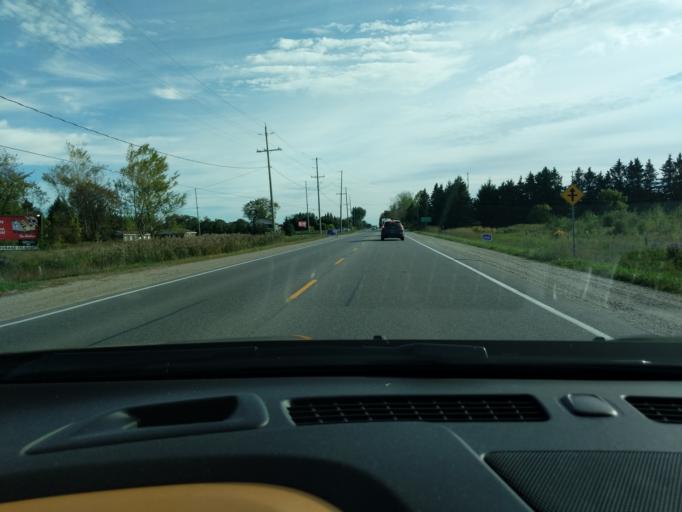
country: CA
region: Ontario
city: Wasaga Beach
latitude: 44.4365
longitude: -80.1001
